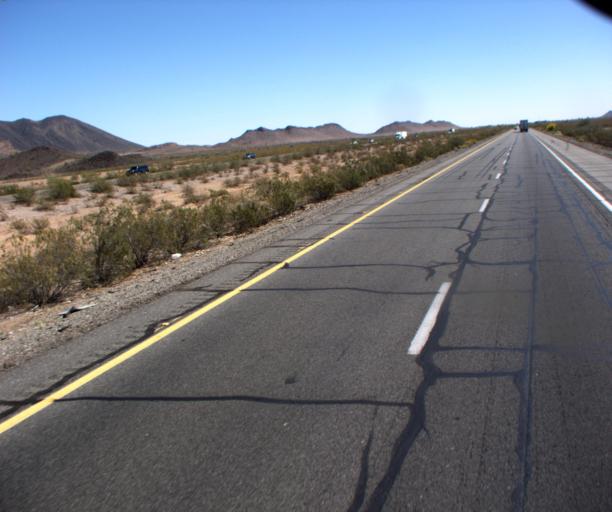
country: US
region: Arizona
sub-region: Maricopa County
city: Buckeye
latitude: 33.5250
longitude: -113.0975
